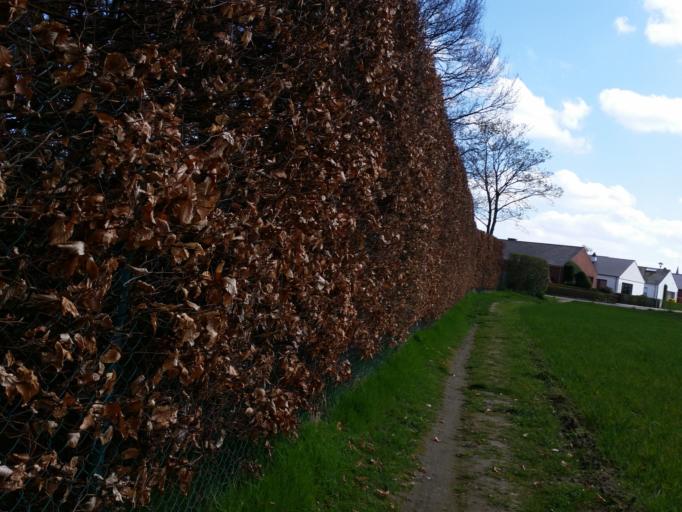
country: BE
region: Flanders
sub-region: Provincie Vlaams-Brabant
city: Boortmeerbeek
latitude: 50.9521
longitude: 4.5775
